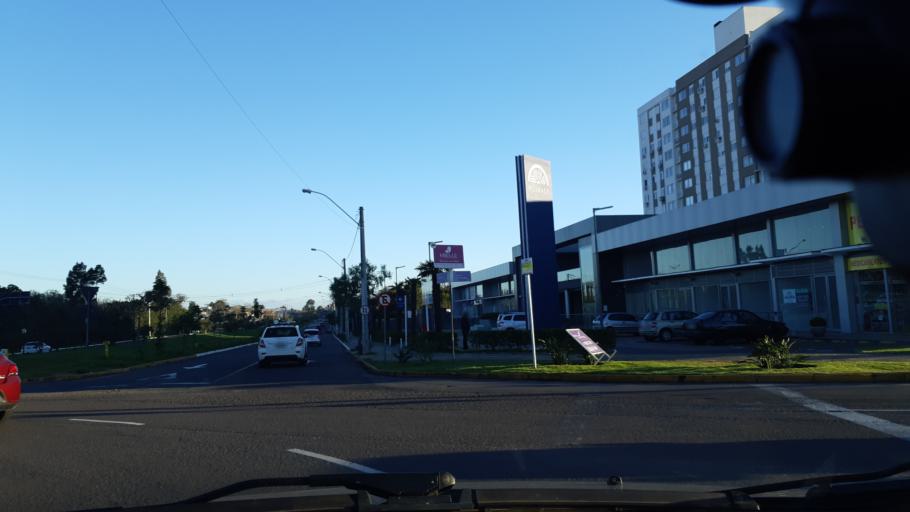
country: BR
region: Rio Grande do Sul
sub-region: Canoas
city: Canoas
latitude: -29.9185
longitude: -51.1551
